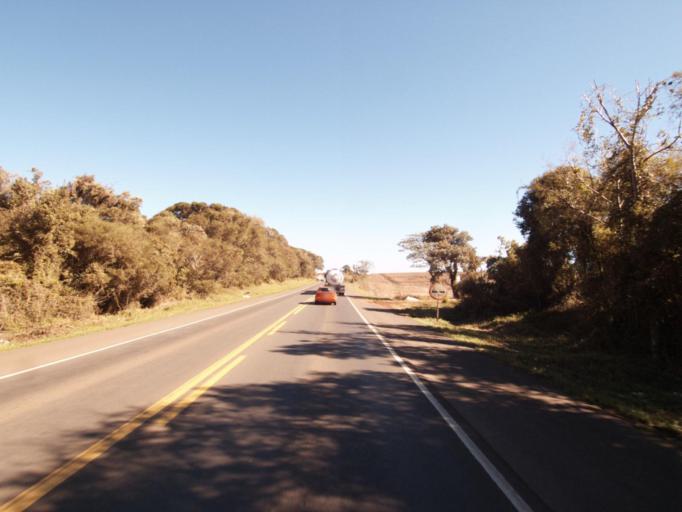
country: BR
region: Santa Catarina
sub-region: Xanxere
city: Xanxere
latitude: -26.8724
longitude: -52.2781
